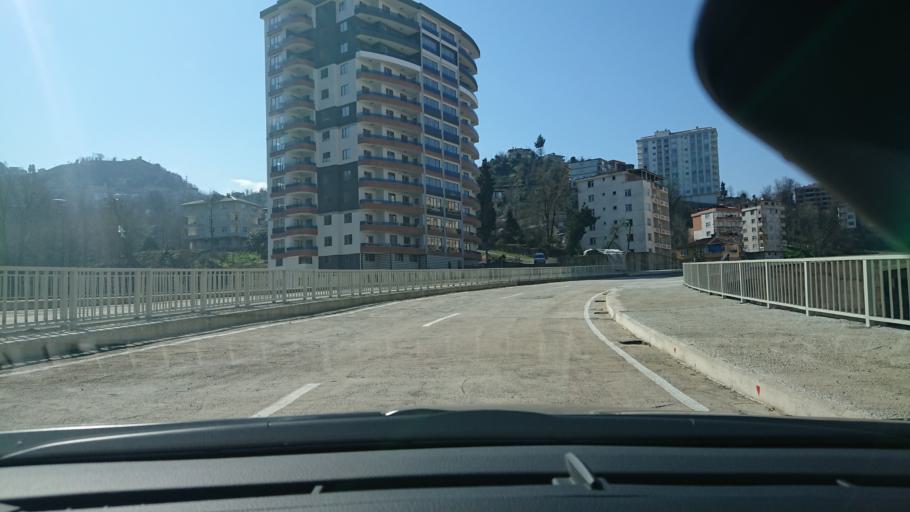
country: TR
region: Rize
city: Rize
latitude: 41.0160
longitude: 40.5173
